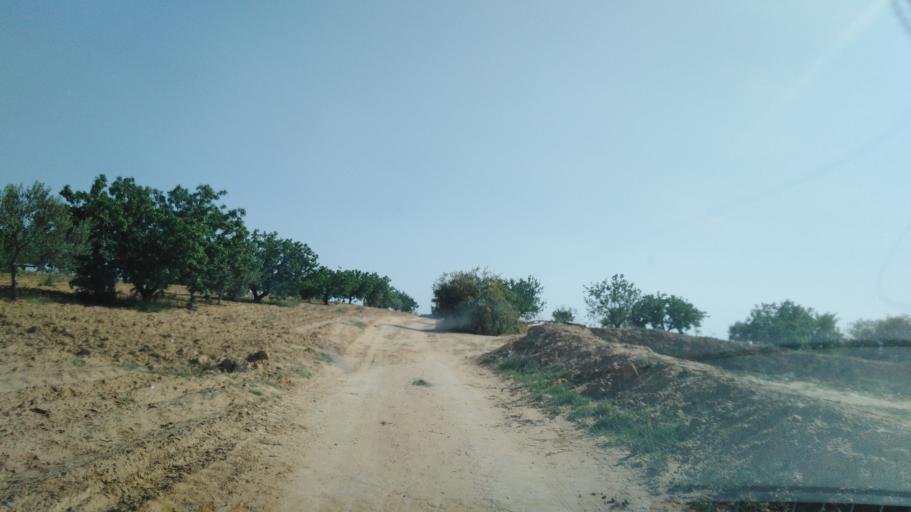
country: TN
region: Safaqis
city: Bi'r `Ali Bin Khalifah
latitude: 34.7859
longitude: 10.3698
